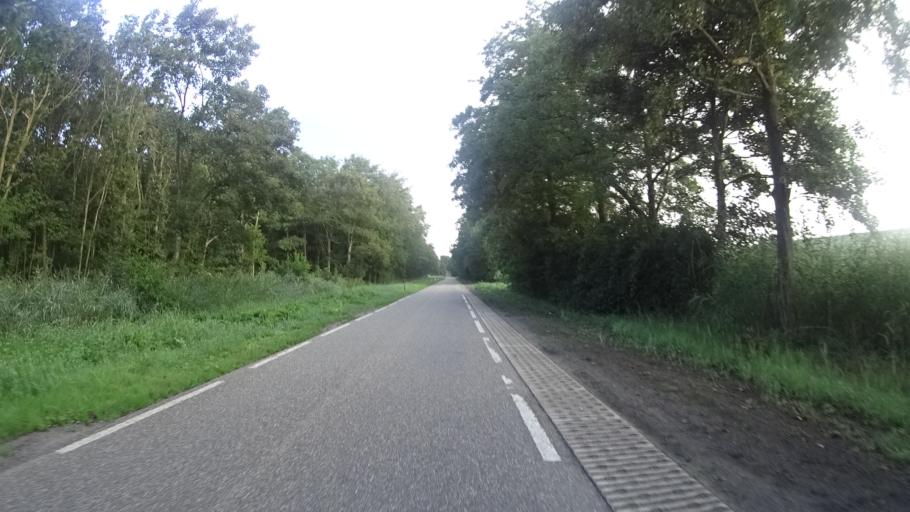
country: NL
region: North Holland
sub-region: Gemeente Hollands Kroon
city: Den Oever
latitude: 52.9149
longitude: 5.0548
